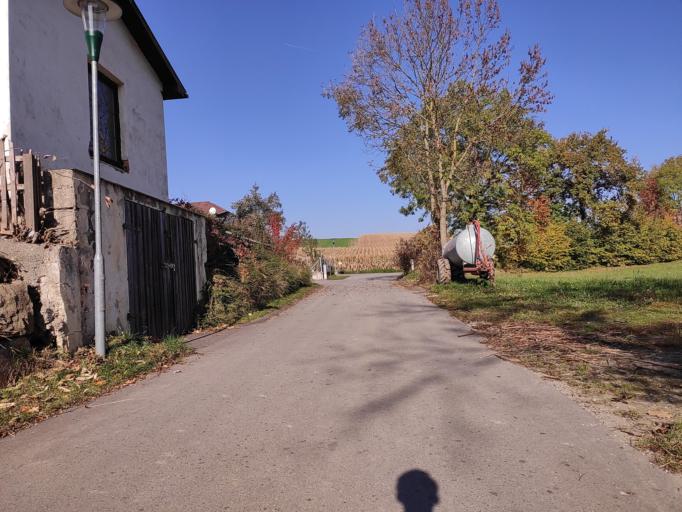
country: AT
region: Lower Austria
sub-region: Politischer Bezirk Sankt Polten
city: Pyhra
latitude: 48.1620
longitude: 15.6861
